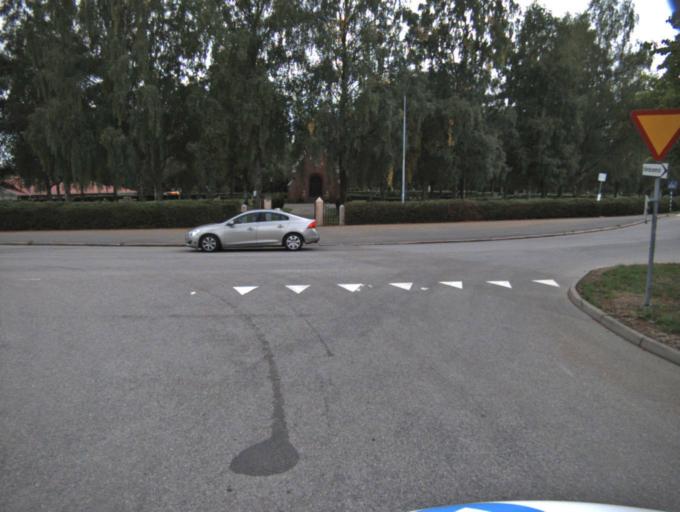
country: SE
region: Vaestra Goetaland
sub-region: Ulricehamns Kommun
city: Ulricehamn
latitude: 57.8049
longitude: 13.4057
